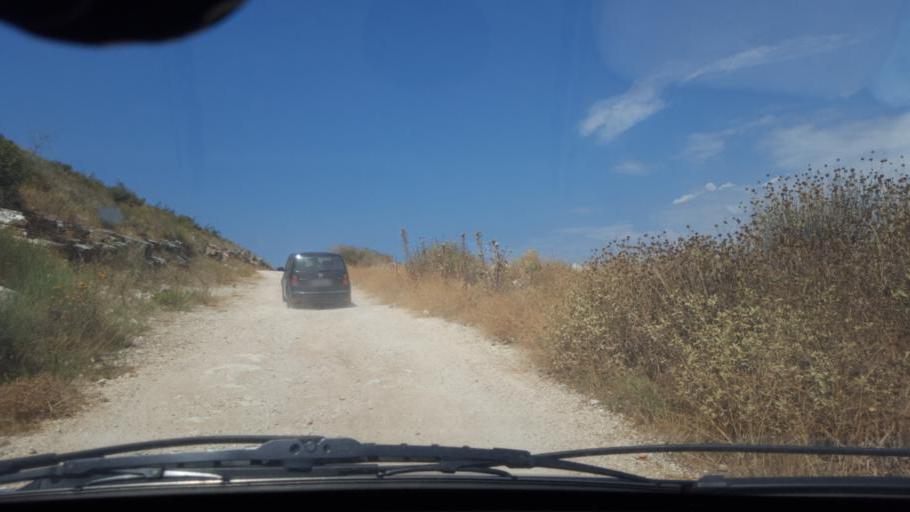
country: AL
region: Vlore
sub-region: Rrethi i Sarandes
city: Sarande
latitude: 39.8422
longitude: 20.0203
